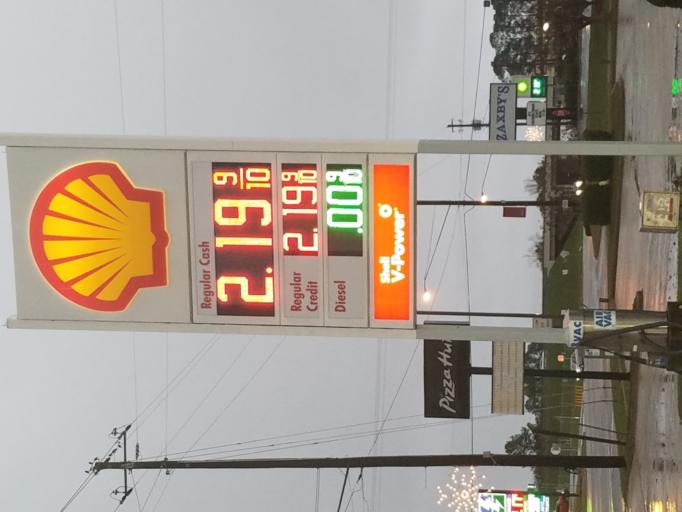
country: US
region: Georgia
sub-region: Turner County
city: Ashburn
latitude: 31.7113
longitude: -83.6406
